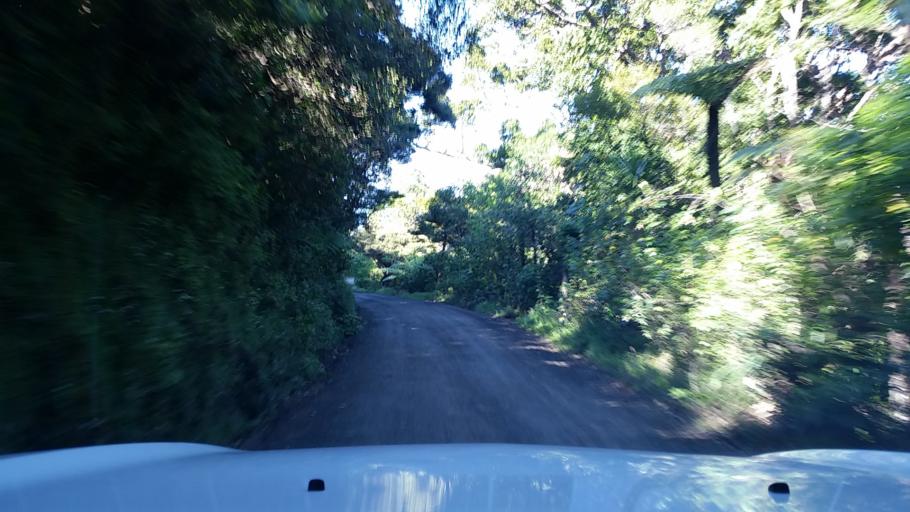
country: NZ
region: Auckland
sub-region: Auckland
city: Titirangi
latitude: -37.0296
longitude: 174.5253
